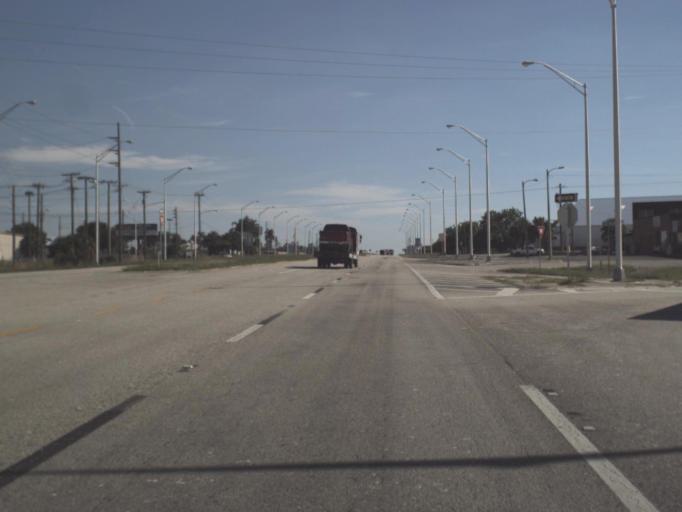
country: US
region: Florida
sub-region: Highlands County
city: Lake Placid
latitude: 27.2684
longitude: -81.3487
